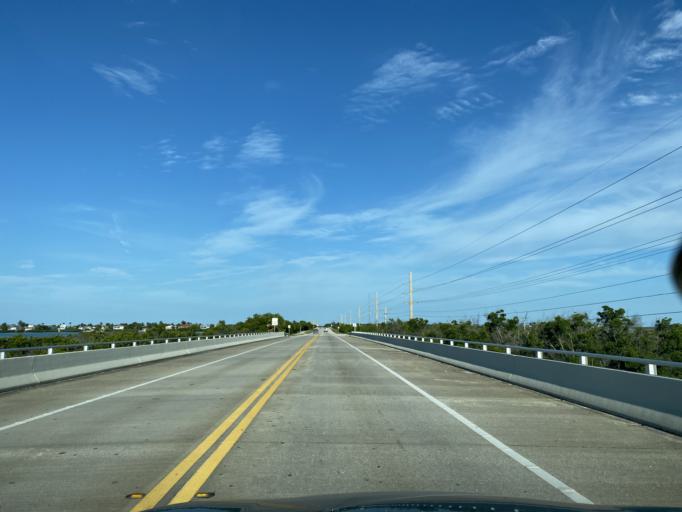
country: US
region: Florida
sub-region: Monroe County
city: Big Pine Key
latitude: 24.6644
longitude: -81.3965
